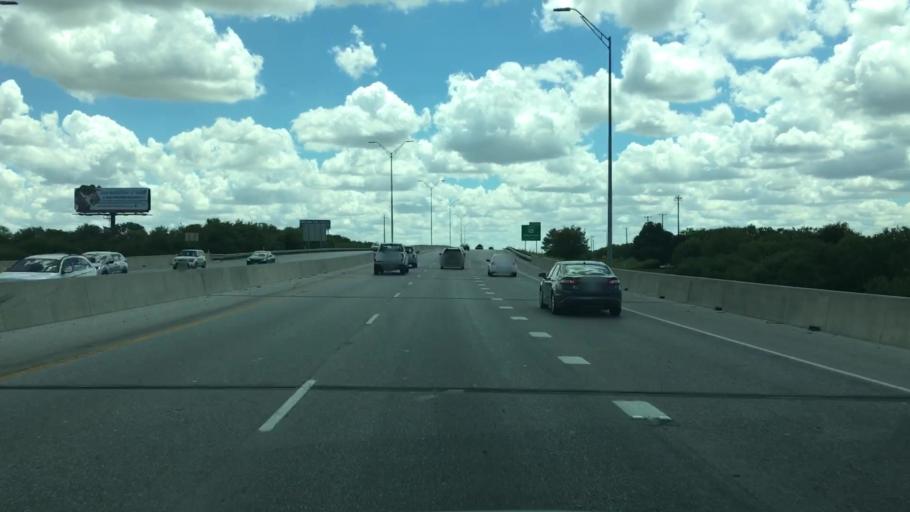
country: US
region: Texas
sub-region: Bexar County
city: China Grove
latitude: 29.3184
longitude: -98.4080
